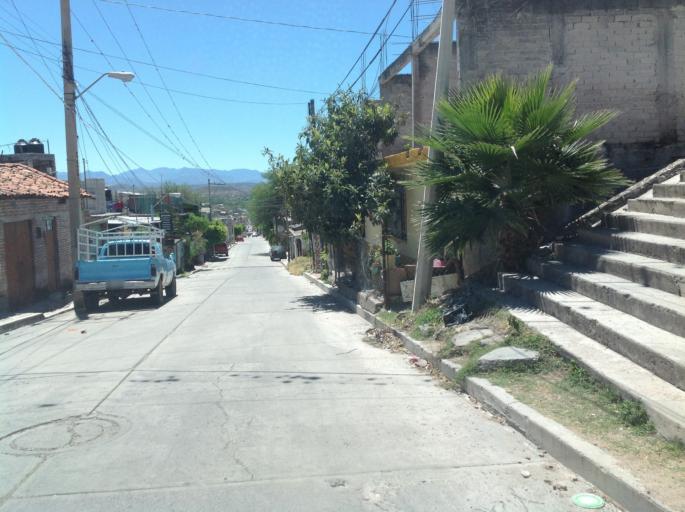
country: MX
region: Oaxaca
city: Ciudad de Huajuapam de Leon
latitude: 17.8153
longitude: -97.7743
